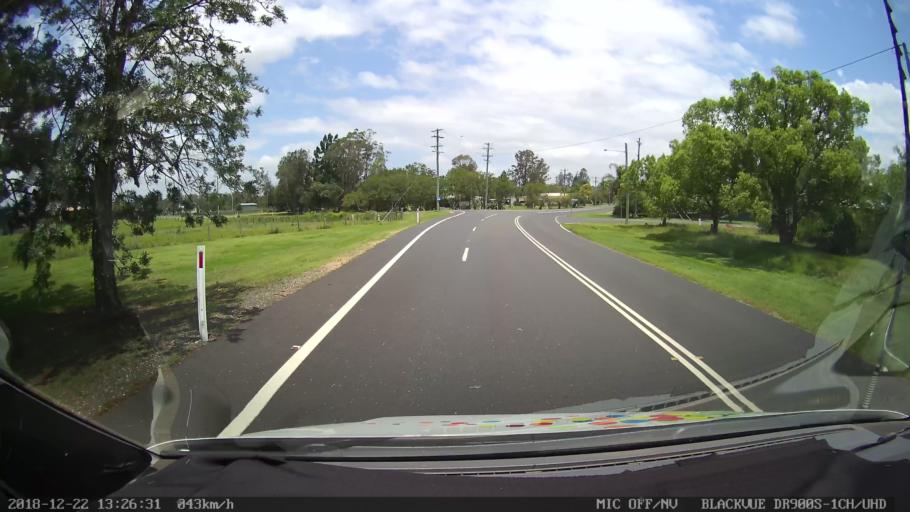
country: AU
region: New South Wales
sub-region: Clarence Valley
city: Coutts Crossing
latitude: -29.8261
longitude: 152.8918
